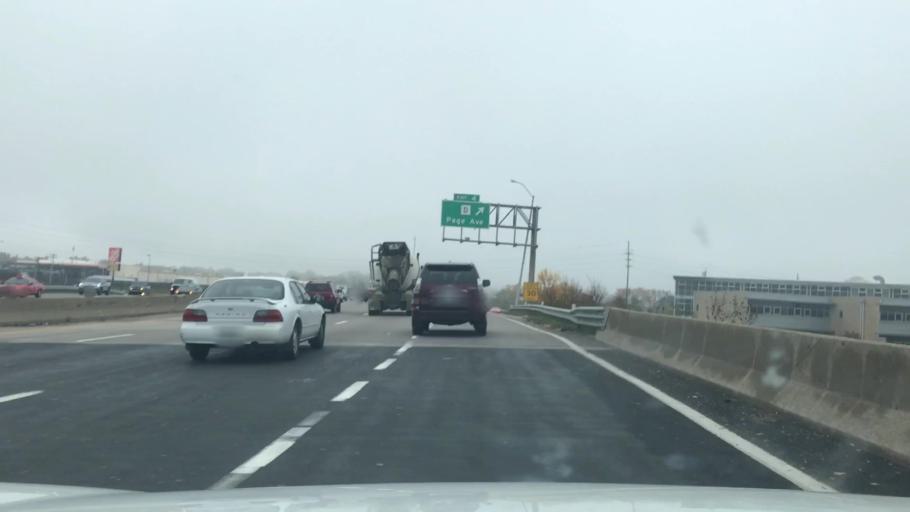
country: US
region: Missouri
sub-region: Saint Louis County
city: Vinita Park
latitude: 38.6842
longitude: -90.3542
